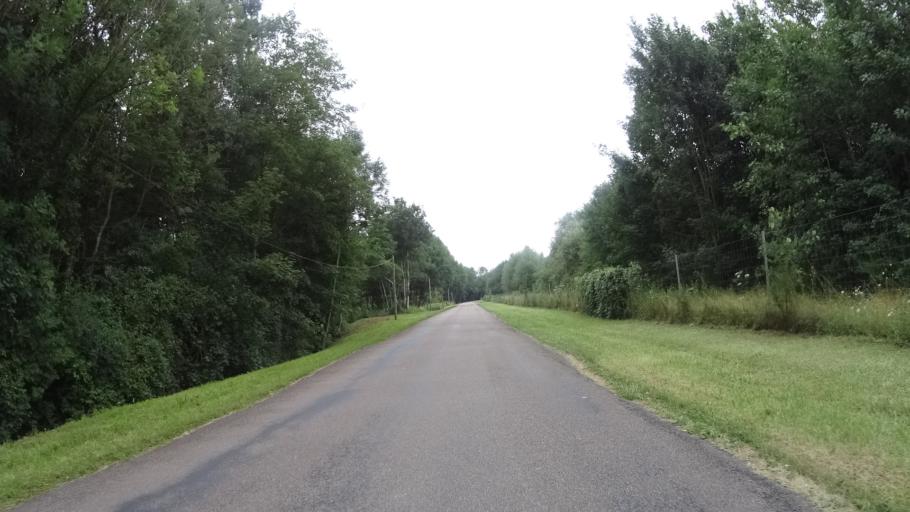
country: FR
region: Champagne-Ardenne
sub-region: Departement de l'Aube
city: Bucheres
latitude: 48.2255
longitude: 4.1250
